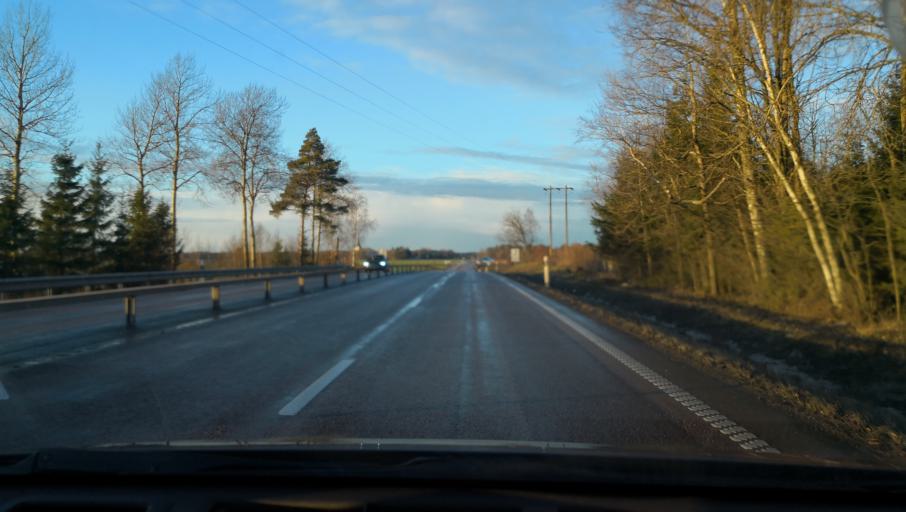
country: SE
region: Vaestmanland
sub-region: Vasteras
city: Hokasen
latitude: 59.7204
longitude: 16.5768
